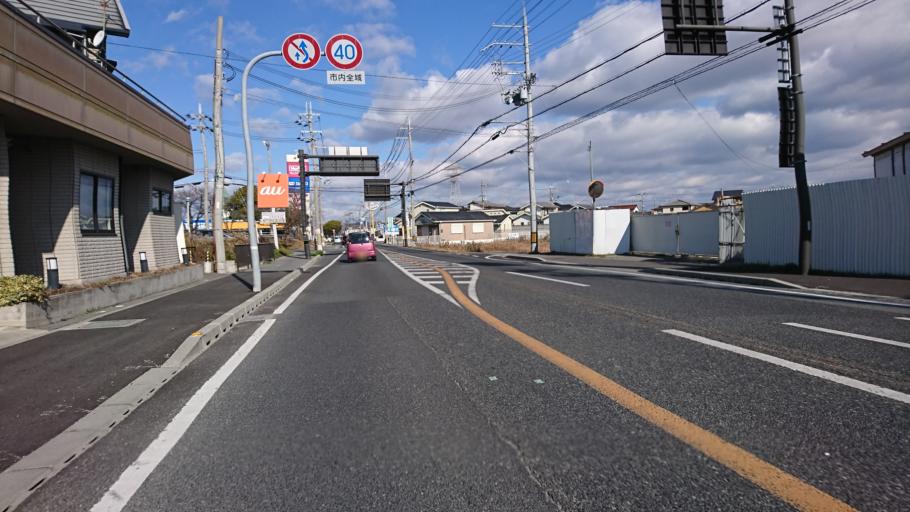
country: JP
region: Hyogo
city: Kakogawacho-honmachi
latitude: 34.7658
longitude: 134.8755
